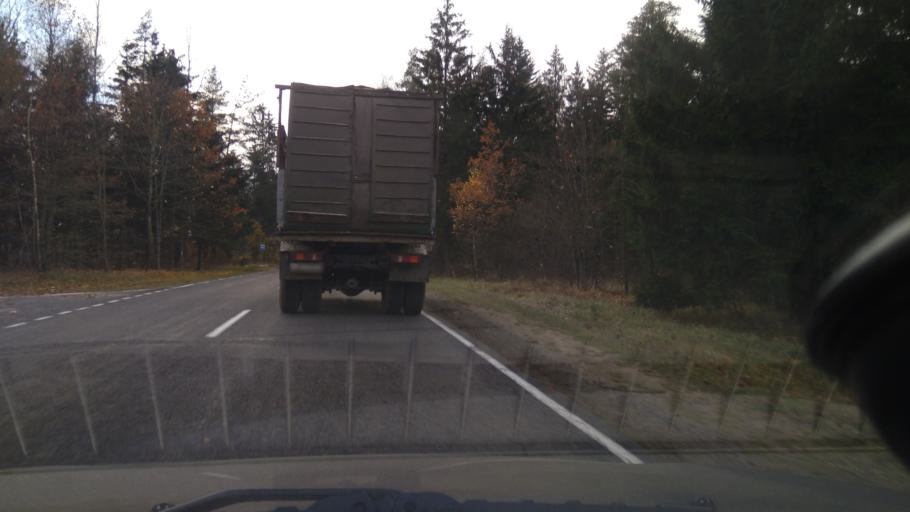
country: BY
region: Minsk
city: Slutsk
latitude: 53.2070
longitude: 27.7721
